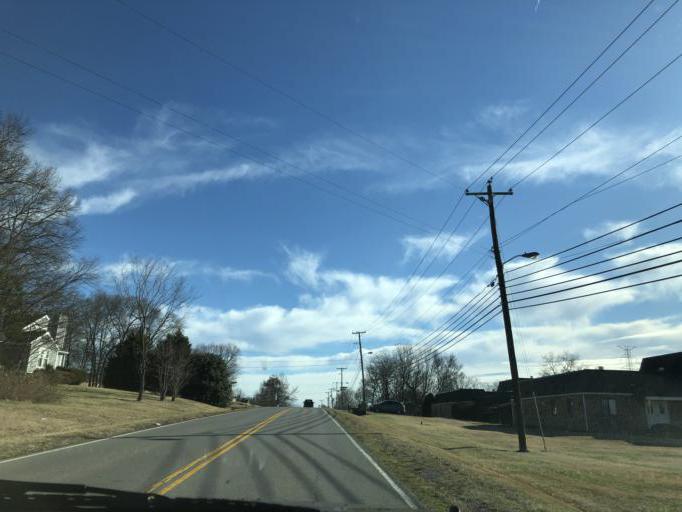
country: US
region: Tennessee
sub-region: Wilson County
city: Green Hill
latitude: 36.1612
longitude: -86.5917
